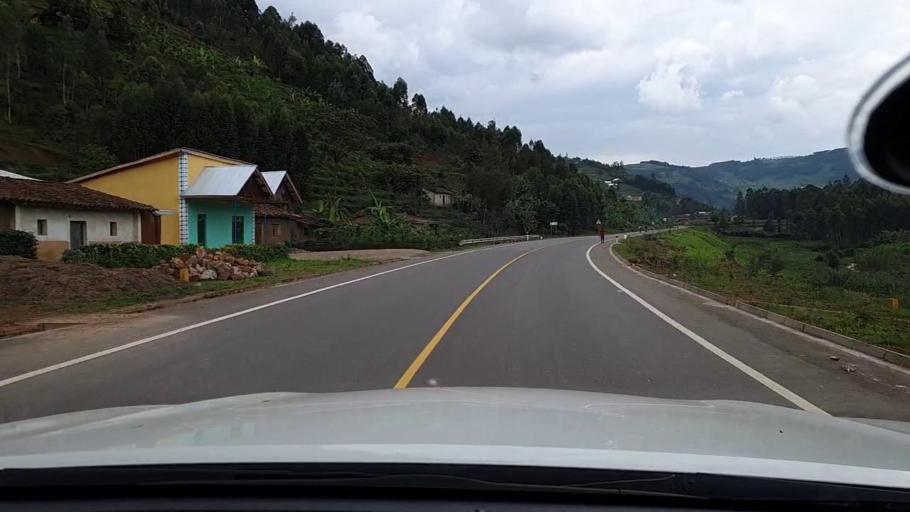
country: RW
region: Northern Province
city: Byumba
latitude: -1.6338
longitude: 29.9279
